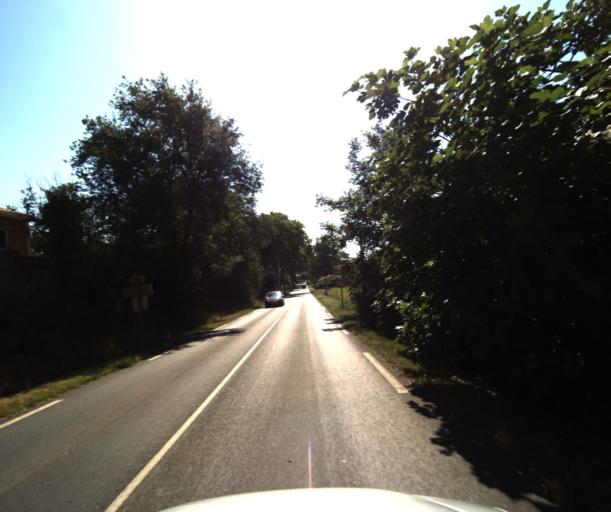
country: FR
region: Midi-Pyrenees
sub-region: Departement de la Haute-Garonne
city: Eaunes
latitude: 43.4226
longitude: 1.3653
